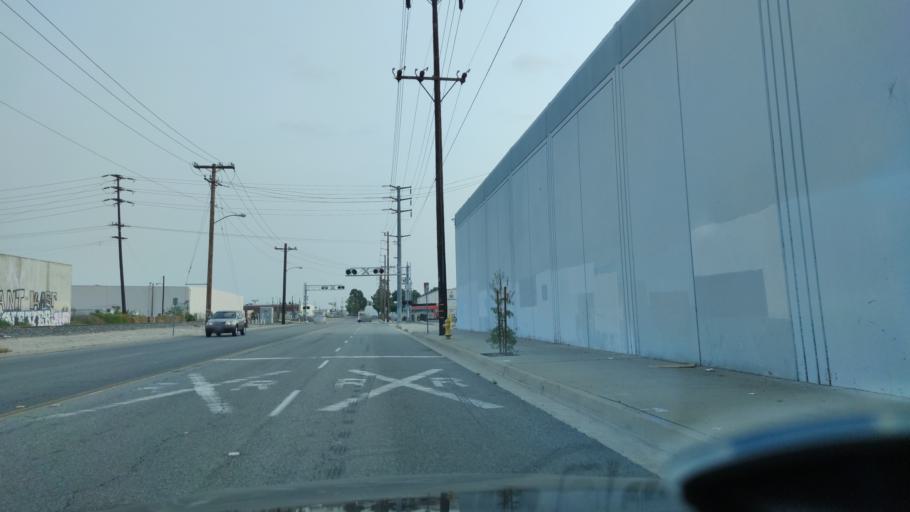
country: US
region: California
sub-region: Los Angeles County
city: Maywood
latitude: 33.9920
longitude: -118.2046
